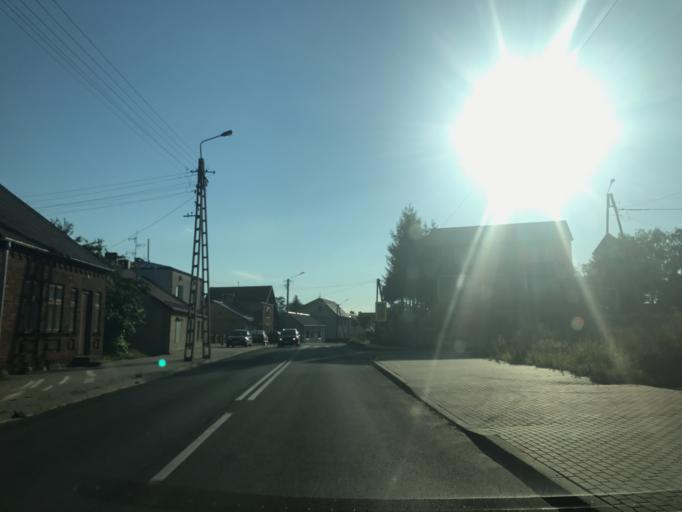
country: PL
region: Greater Poland Voivodeship
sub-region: Powiat turecki
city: Tuliszkow
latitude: 52.0765
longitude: 18.2902
